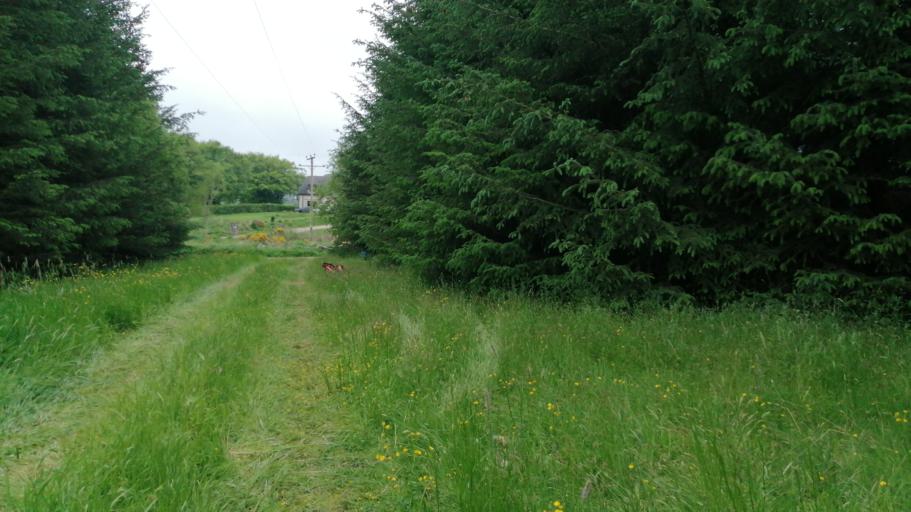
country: GB
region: Scotland
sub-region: Moray
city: Cullen
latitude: 57.5767
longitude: -2.7899
